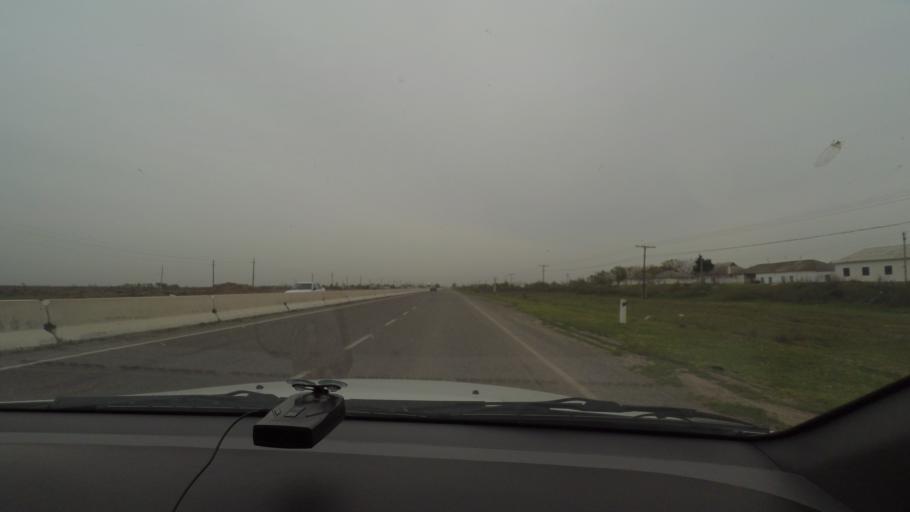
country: UZ
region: Sirdaryo
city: Guliston
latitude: 40.4954
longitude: 68.6376
